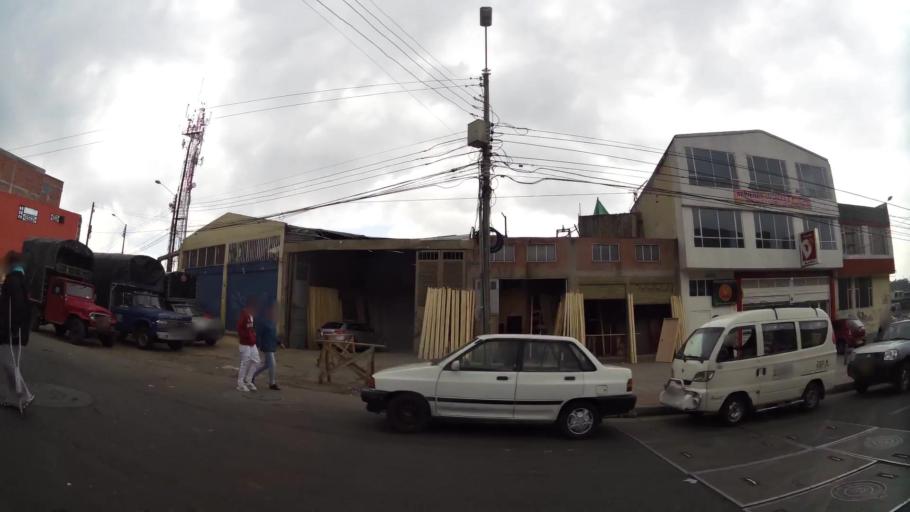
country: CO
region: Bogota D.C.
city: Bogota
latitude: 4.5716
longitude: -74.0974
